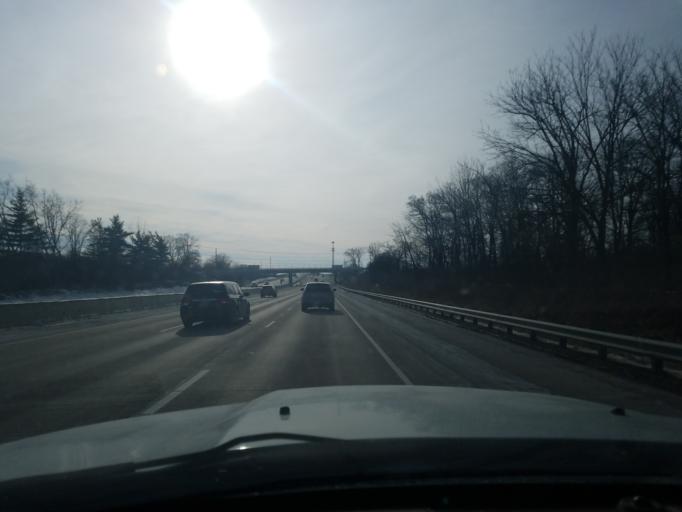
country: US
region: Indiana
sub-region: Allen County
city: Fort Wayne
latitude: 41.0905
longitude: -85.2195
